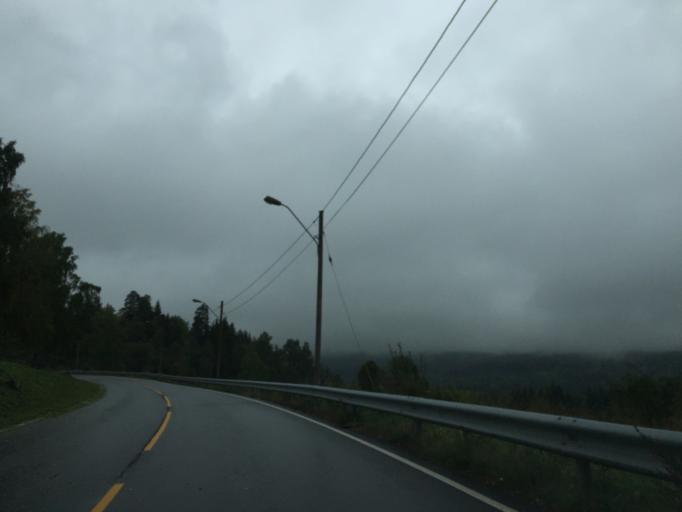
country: NO
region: Akershus
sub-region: Baerum
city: Lysaker
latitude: 60.0064
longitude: 10.6215
